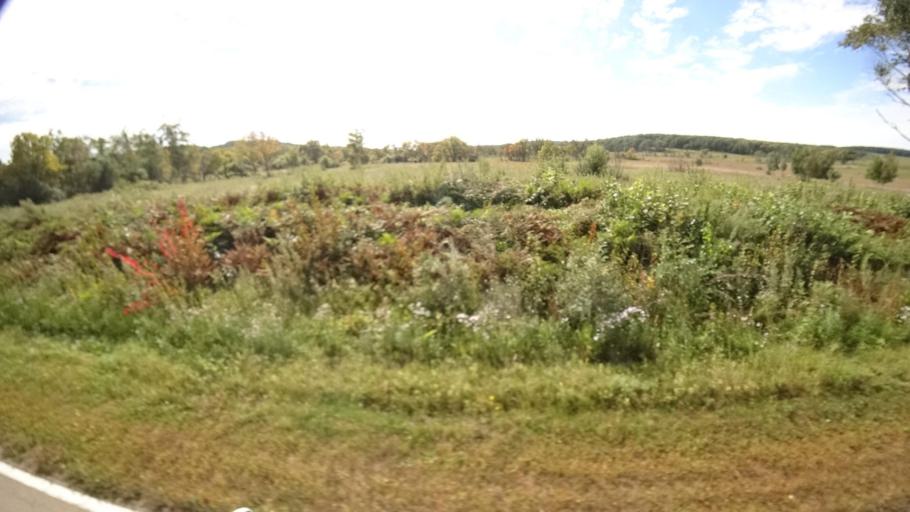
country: RU
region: Primorskiy
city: Yakovlevka
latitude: 44.4076
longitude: 133.5909
